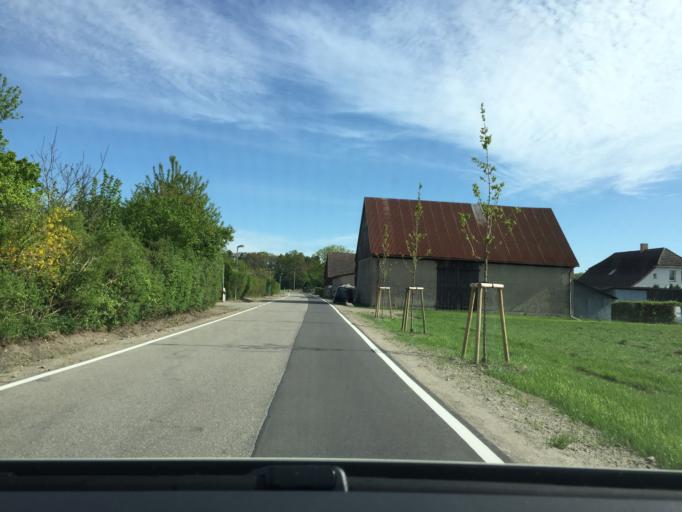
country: DE
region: Mecklenburg-Vorpommern
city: Torgelow
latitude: 53.6448
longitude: 14.0273
